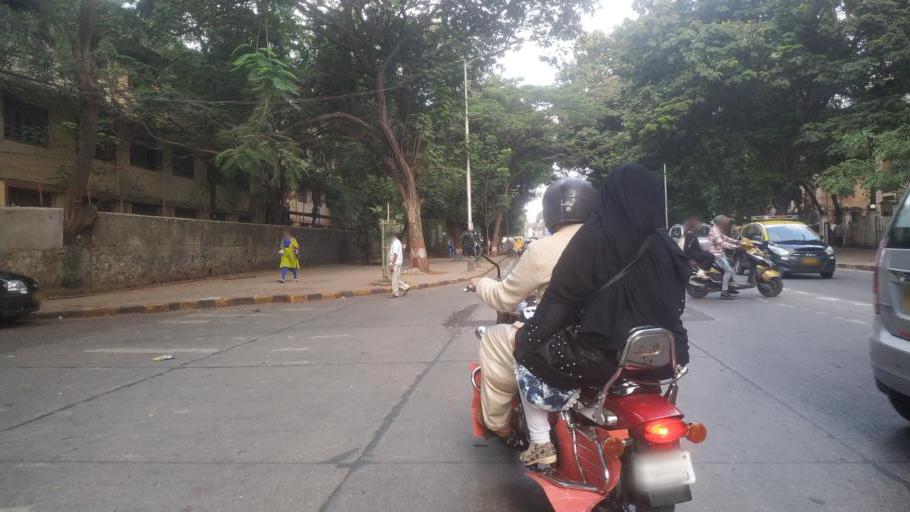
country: IN
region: Maharashtra
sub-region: Mumbai Suburban
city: Mumbai
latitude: 19.0197
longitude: 72.8547
